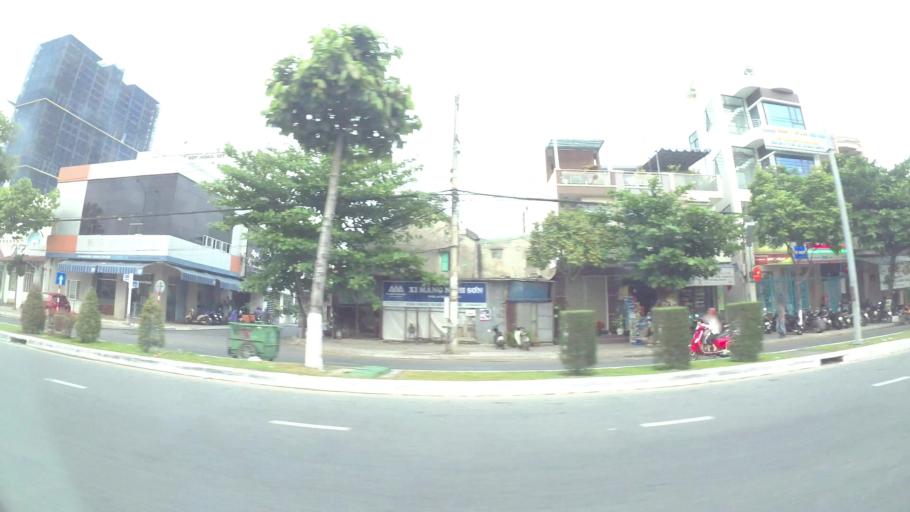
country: VN
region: Da Nang
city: Son Tra
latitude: 16.0598
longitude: 108.2350
